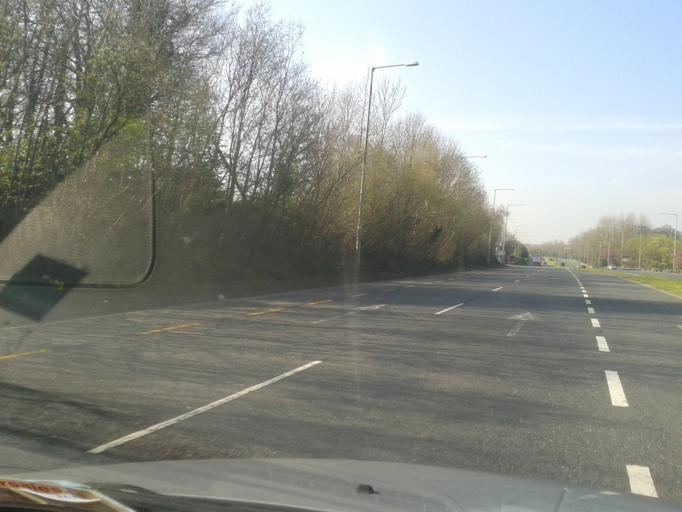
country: IE
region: Leinster
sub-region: Fingal County
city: Swords
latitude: 53.4726
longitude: -6.2102
